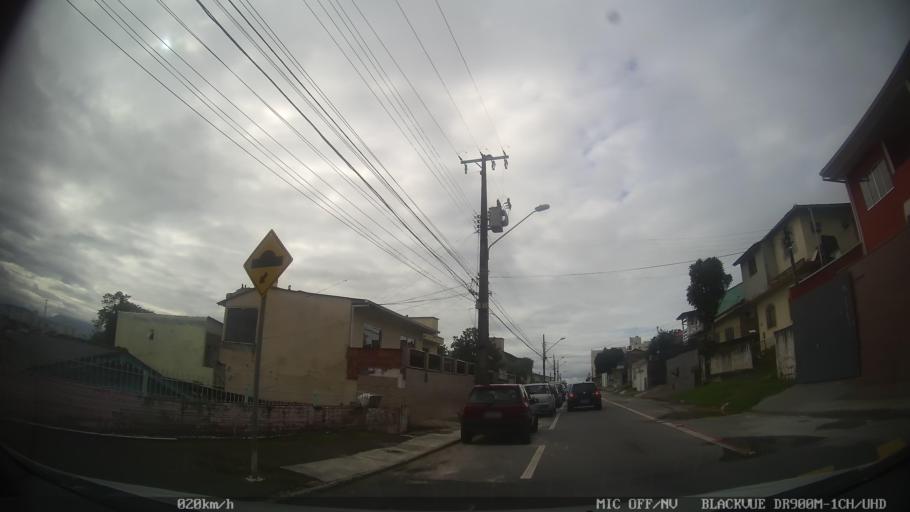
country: BR
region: Santa Catarina
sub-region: Sao Jose
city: Campinas
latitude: -27.5707
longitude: -48.6238
